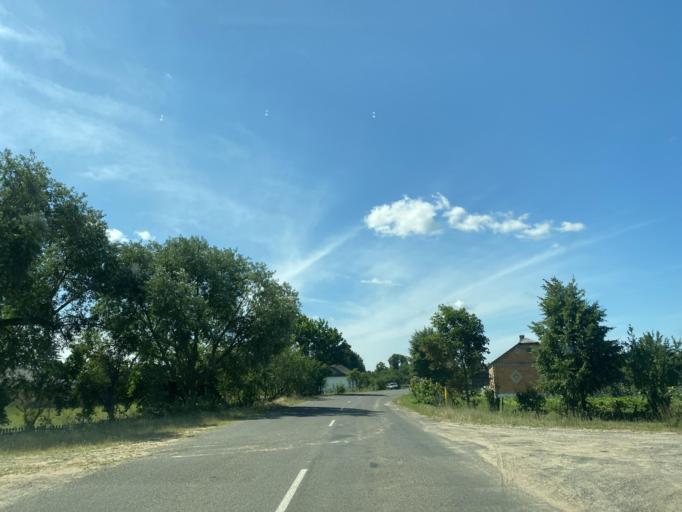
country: BY
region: Brest
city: Ivanava
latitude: 52.1837
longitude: 25.6071
